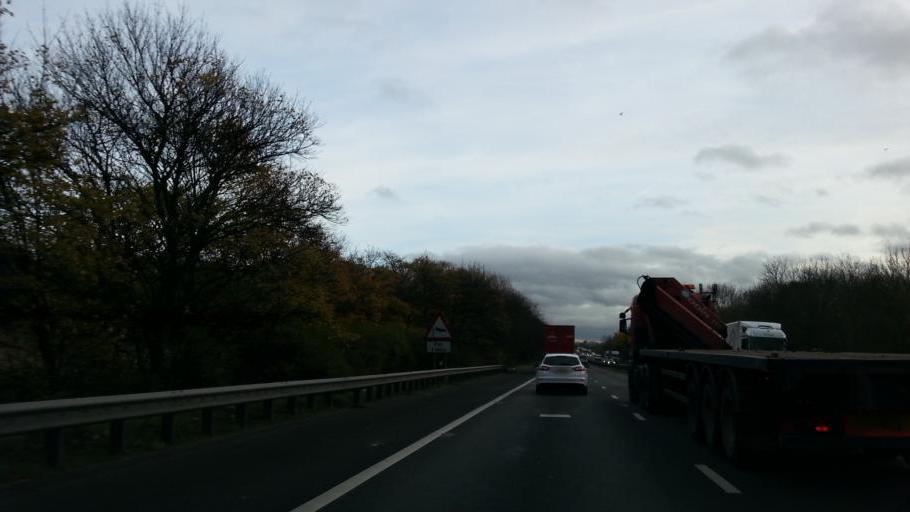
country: GB
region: England
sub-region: Doncaster
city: Marr
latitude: 53.5499
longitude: -1.2127
